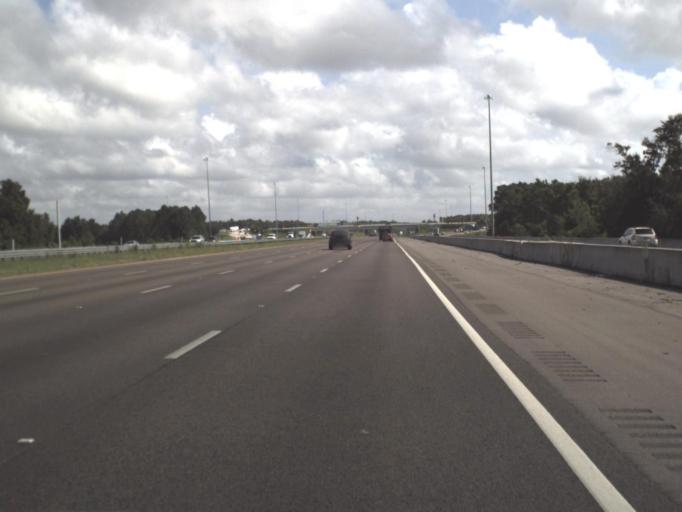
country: US
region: Florida
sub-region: Hillsborough County
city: Pebble Creek
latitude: 28.1867
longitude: -82.3870
